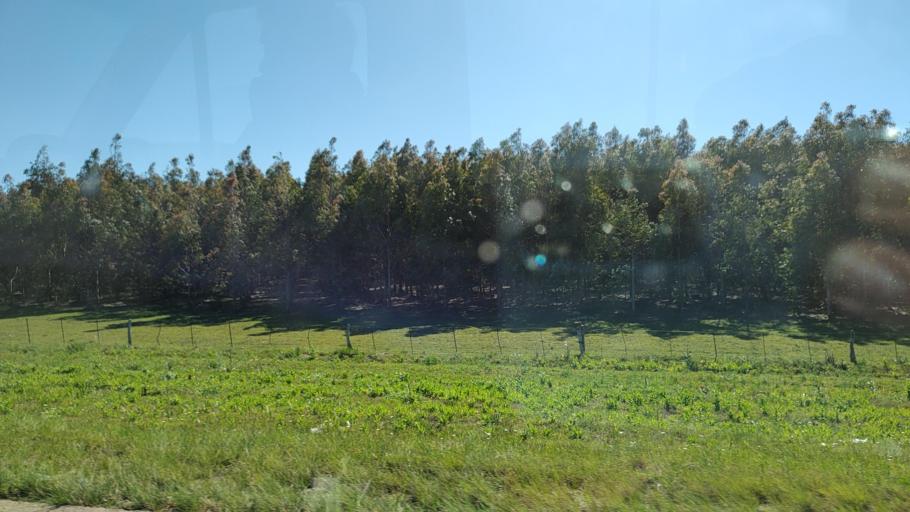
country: AR
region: Entre Rios
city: Villa Elisa
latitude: -32.0158
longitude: -58.2861
